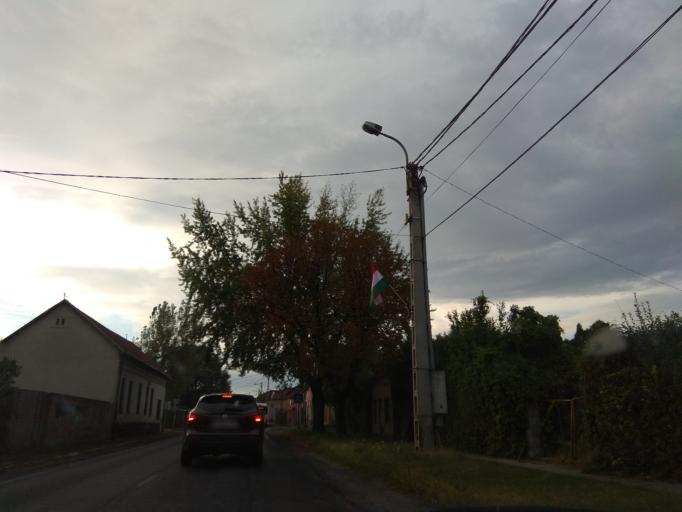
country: HU
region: Borsod-Abauj-Zemplen
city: Miskolc
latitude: 48.0943
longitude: 20.8051
